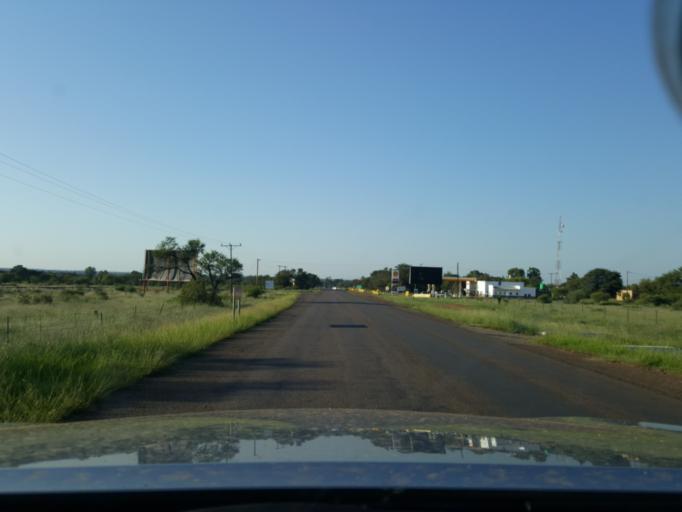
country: BW
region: South East
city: Janeng
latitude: -25.6296
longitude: 25.5744
